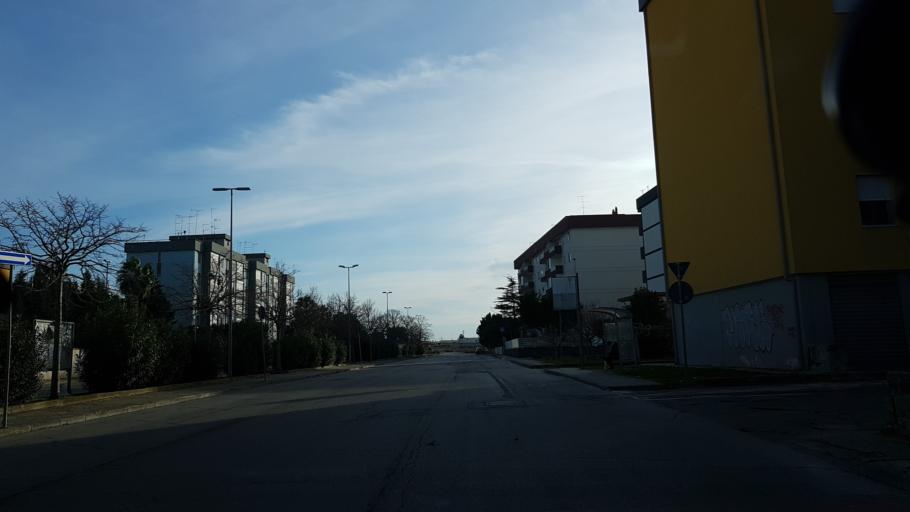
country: IT
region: Apulia
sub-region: Provincia di Brindisi
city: Brindisi
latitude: 40.6179
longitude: 17.9253
